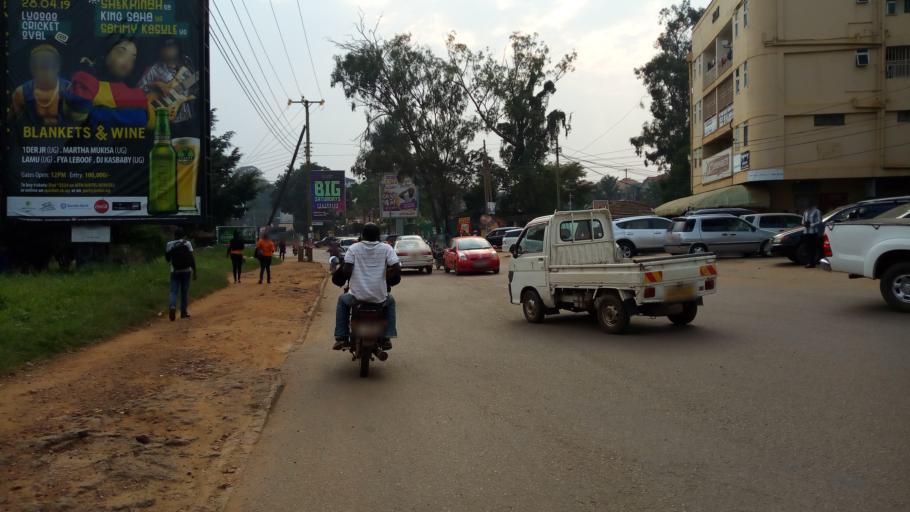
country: UG
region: Central Region
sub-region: Kampala District
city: Kampala
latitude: 0.3205
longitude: 32.6189
